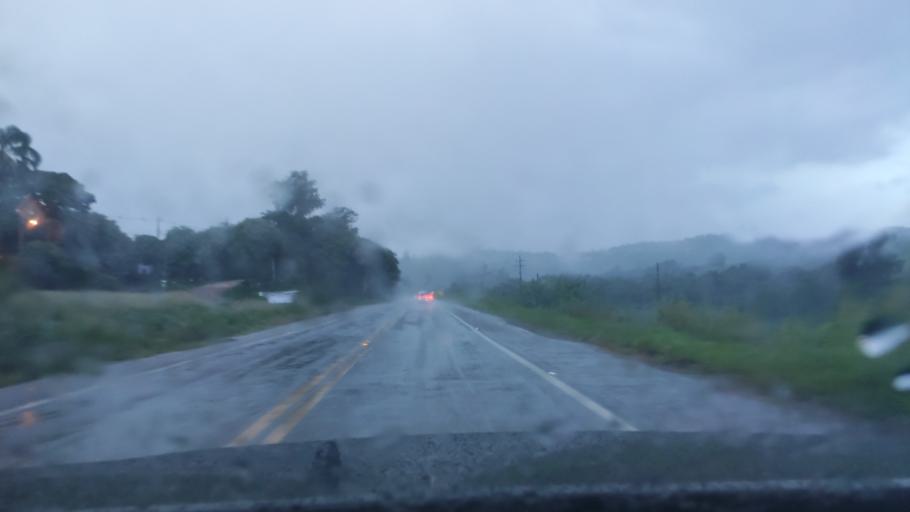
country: BR
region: Sao Paulo
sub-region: Braganca Paulista
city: Braganca Paulista
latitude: -22.7978
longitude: -46.5549
